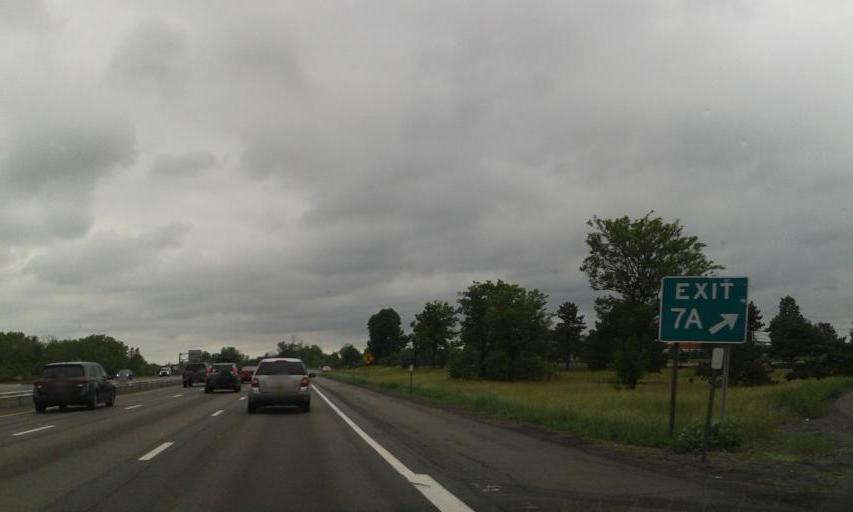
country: US
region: New York
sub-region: Erie County
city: Williamsville
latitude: 42.9606
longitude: -78.7666
